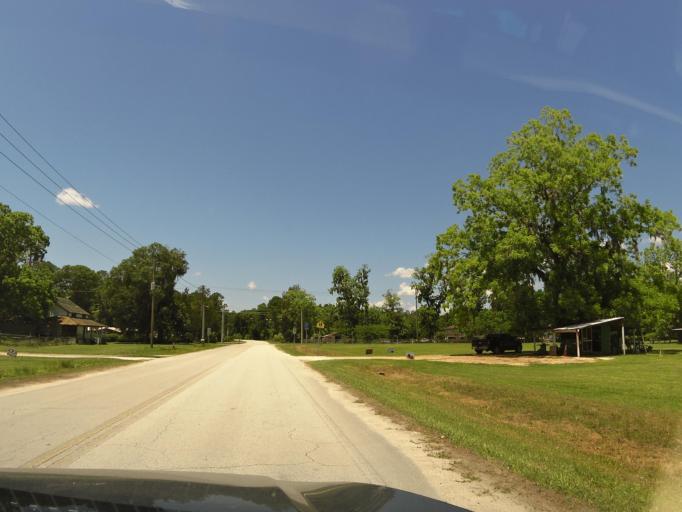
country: US
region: Florida
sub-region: Bradford County
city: Starke
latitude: 30.0441
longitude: -82.0755
